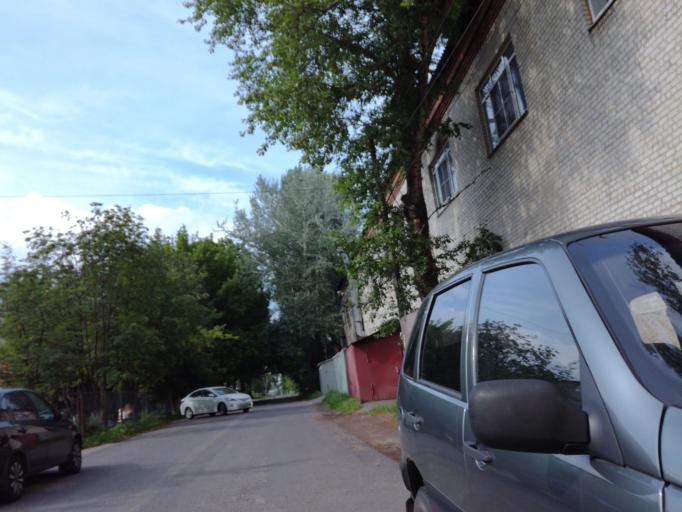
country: RU
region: Kursk
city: Kursk
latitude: 51.7453
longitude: 36.1816
